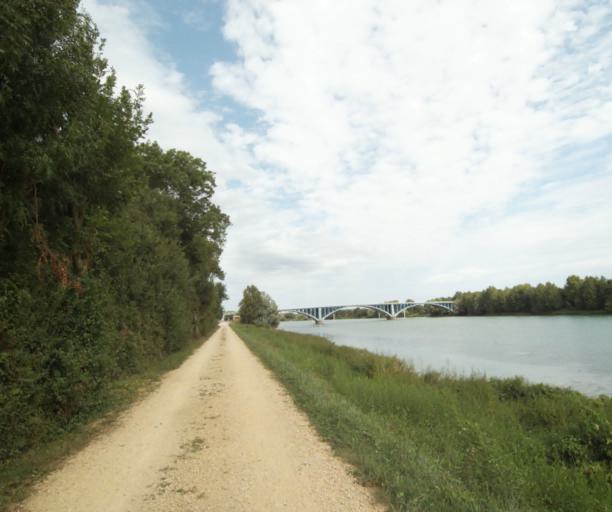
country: FR
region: Bourgogne
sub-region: Departement de Saone-et-Loire
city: Tournus
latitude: 46.5530
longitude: 4.9191
